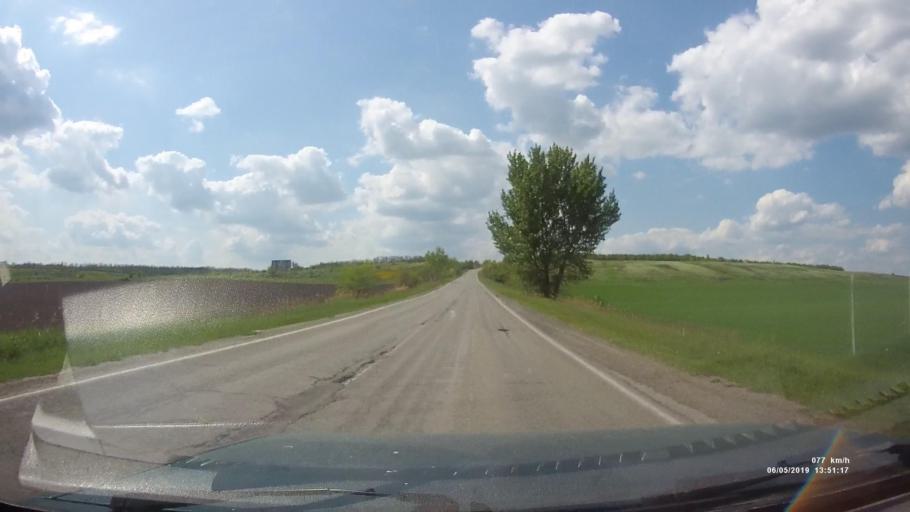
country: RU
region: Rostov
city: Melikhovskaya
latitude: 47.6565
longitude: 40.4944
